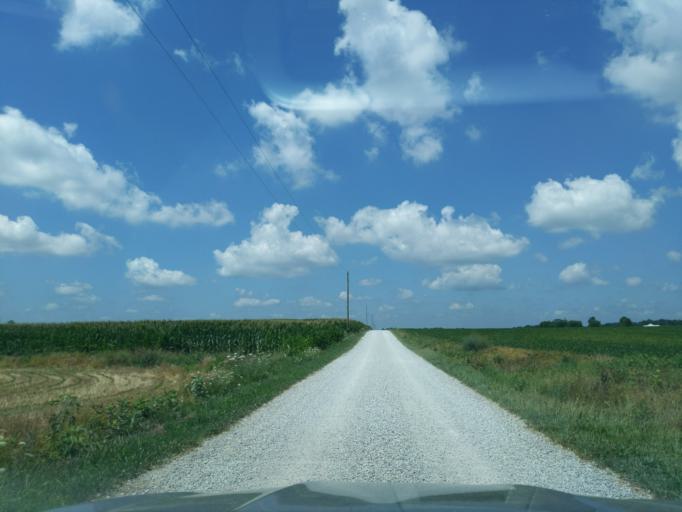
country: US
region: Indiana
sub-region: Ripley County
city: Osgood
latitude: 39.2208
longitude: -85.3679
